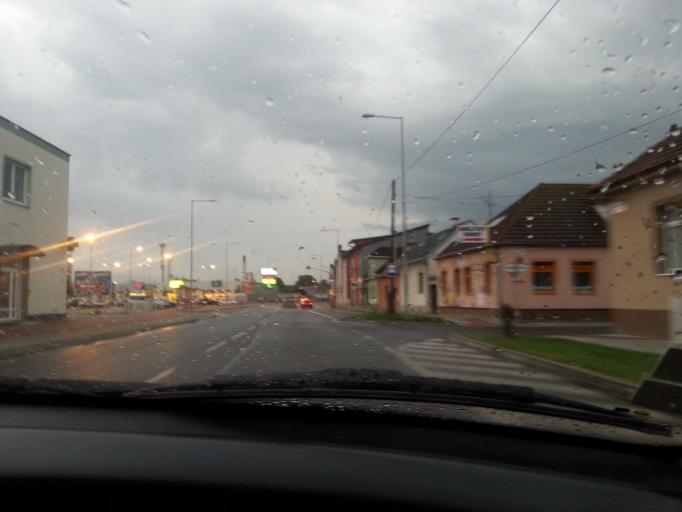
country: SK
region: Trenciansky
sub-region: Okres Nove Mesto nad Vahom
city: Nove Mesto nad Vahom
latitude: 48.7583
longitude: 17.8362
